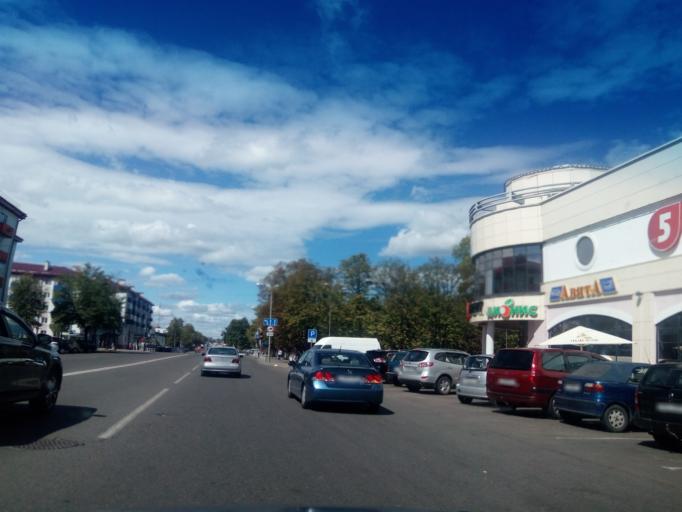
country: BY
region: Vitebsk
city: Polatsk
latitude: 55.4904
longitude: 28.7819
